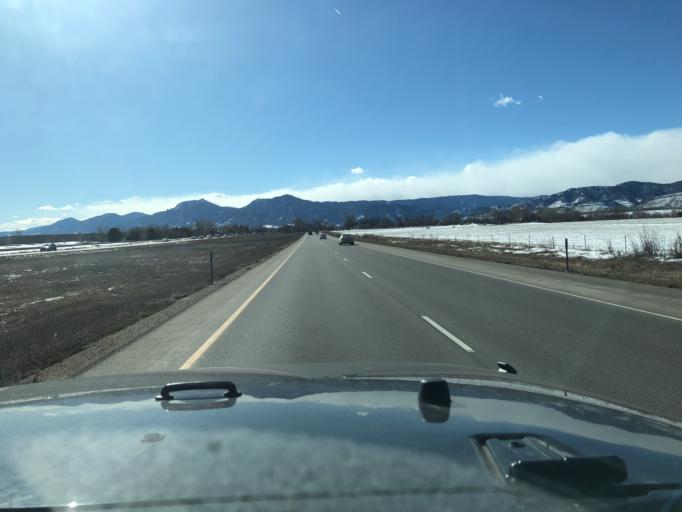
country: US
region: Colorado
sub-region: Boulder County
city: Gunbarrel
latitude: 40.0649
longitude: -105.2173
